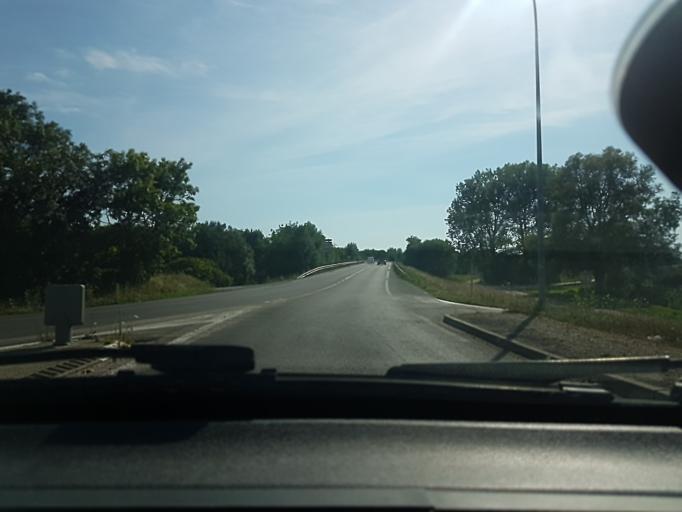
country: FR
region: Bourgogne
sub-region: Departement de Saone-et-Loire
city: Saint-Marcel
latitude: 46.7629
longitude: 4.8928
